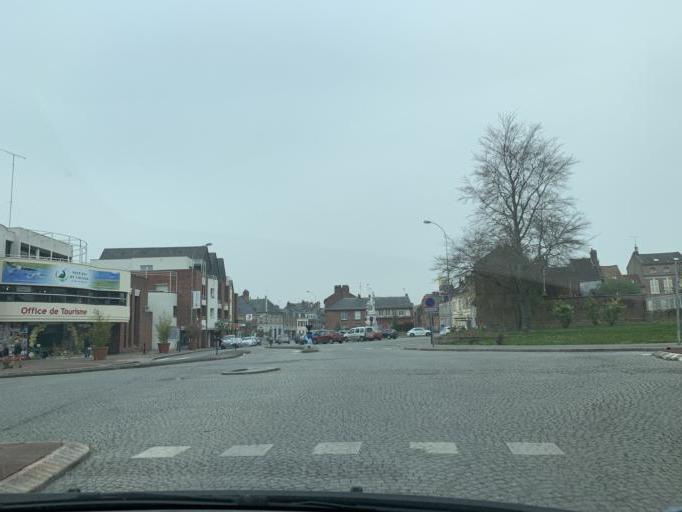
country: FR
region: Picardie
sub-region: Departement de la Somme
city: Abbeville
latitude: 50.1069
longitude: 1.8327
